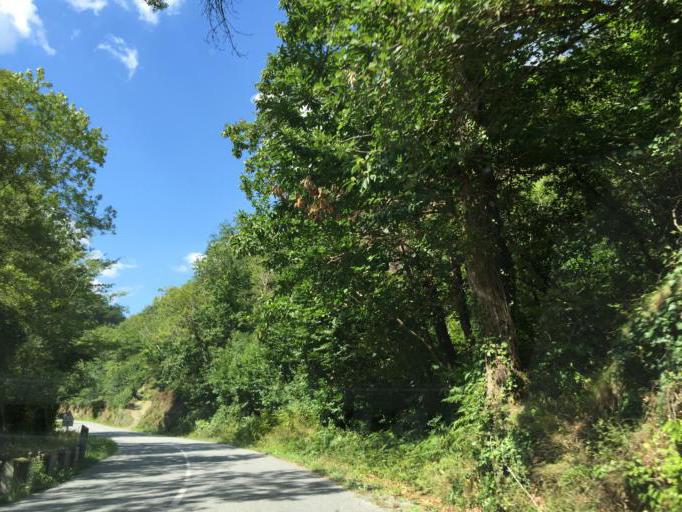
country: FR
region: Midi-Pyrenees
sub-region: Departement de l'Aveyron
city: Saint-Christophe-Vallon
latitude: 44.5727
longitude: 2.4086
